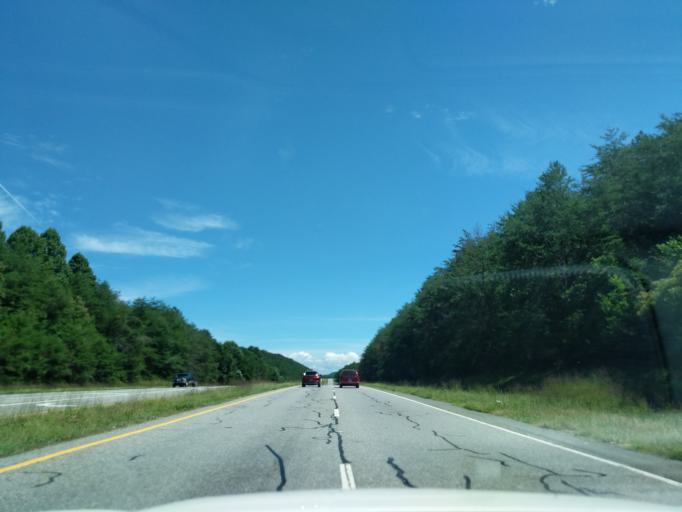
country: US
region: Georgia
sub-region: Fannin County
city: Blue Ridge
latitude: 34.8923
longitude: -84.2436
